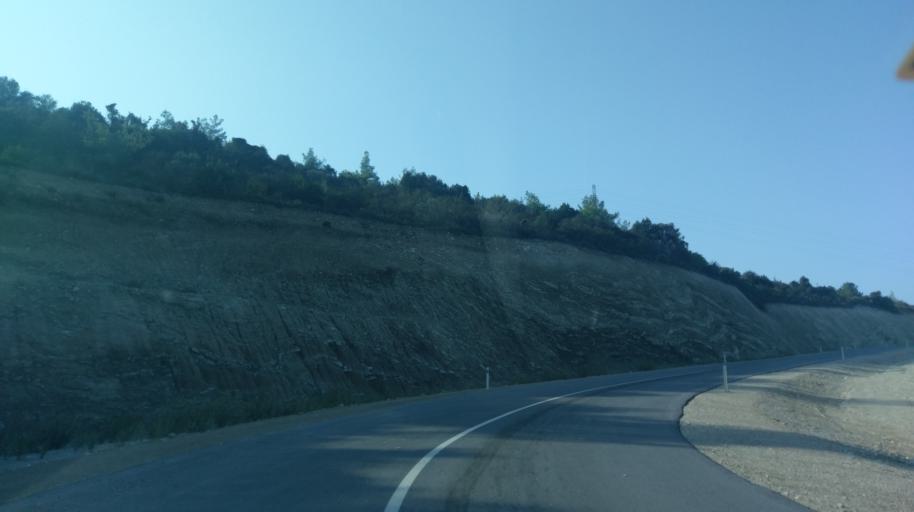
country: CY
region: Ammochostos
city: Leonarisso
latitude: 35.5357
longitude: 34.2403
